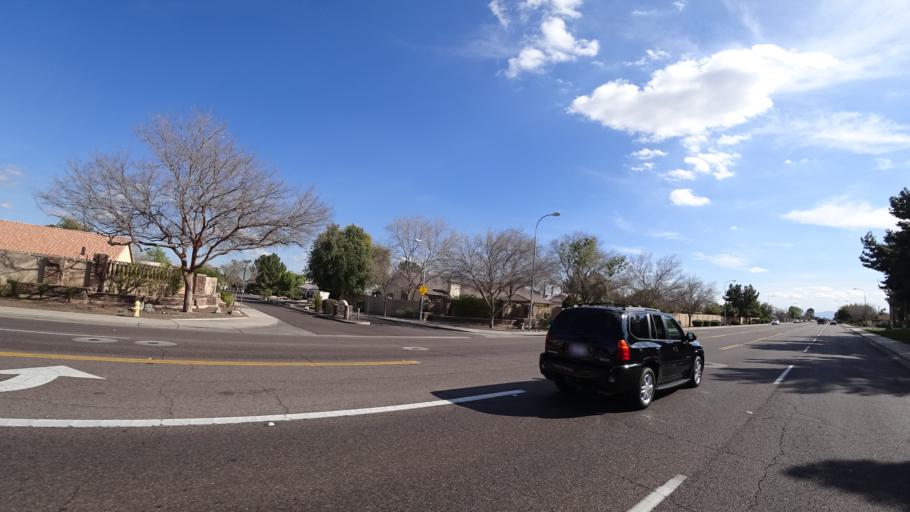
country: US
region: Arizona
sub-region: Maricopa County
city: Peoria
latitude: 33.6209
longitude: -112.2201
